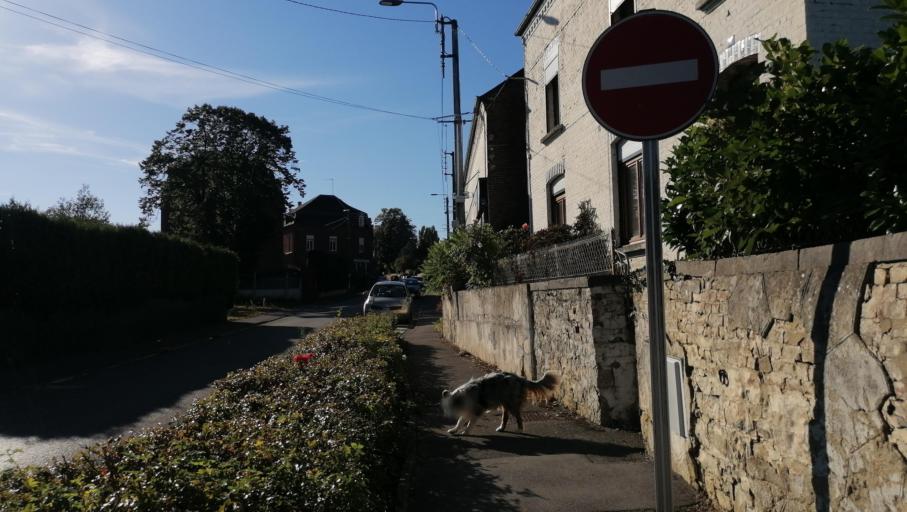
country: FR
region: Nord-Pas-de-Calais
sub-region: Departement du Nord
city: Sains-du-Nord
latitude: 50.0937
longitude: 4.0104
